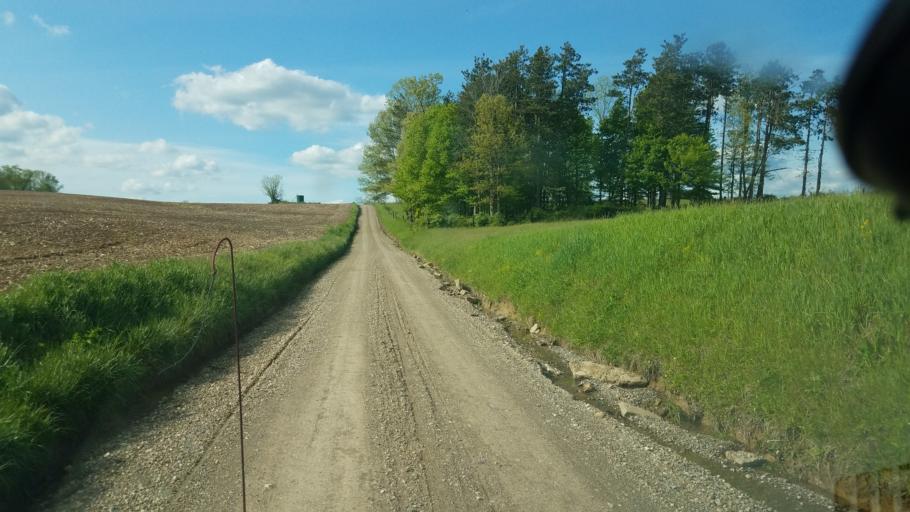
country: US
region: Ohio
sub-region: Knox County
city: Oak Hill
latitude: 40.2924
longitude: -82.1729
